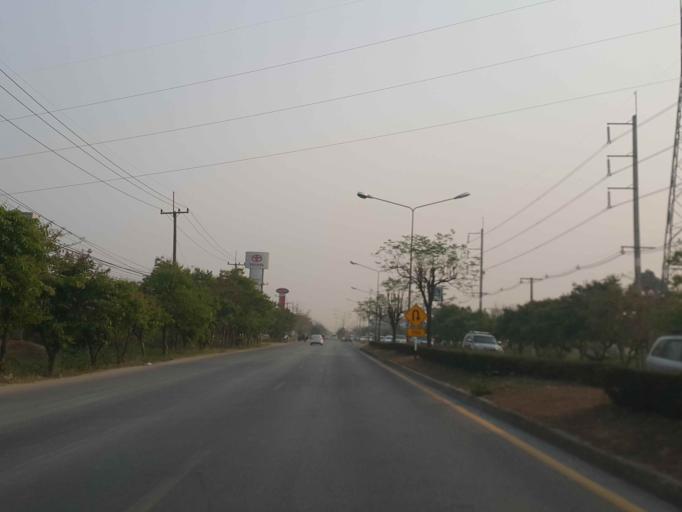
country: TH
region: Chiang Mai
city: San Sai
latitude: 18.8587
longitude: 99.0146
